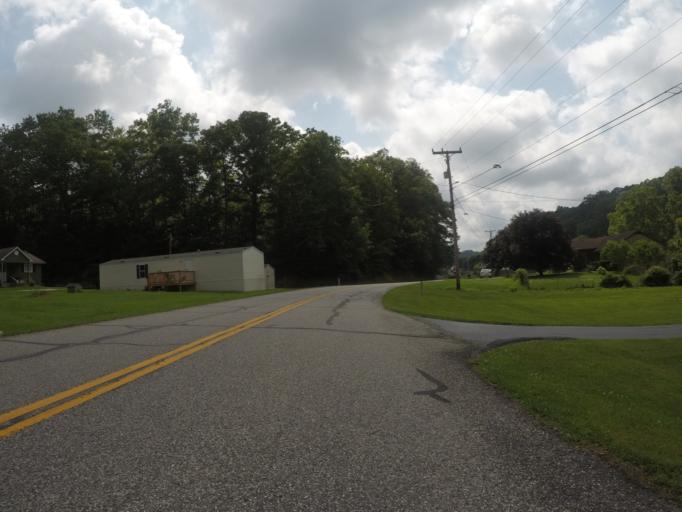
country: US
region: Kentucky
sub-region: Boyd County
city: Meads
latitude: 38.4121
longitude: -82.6735
